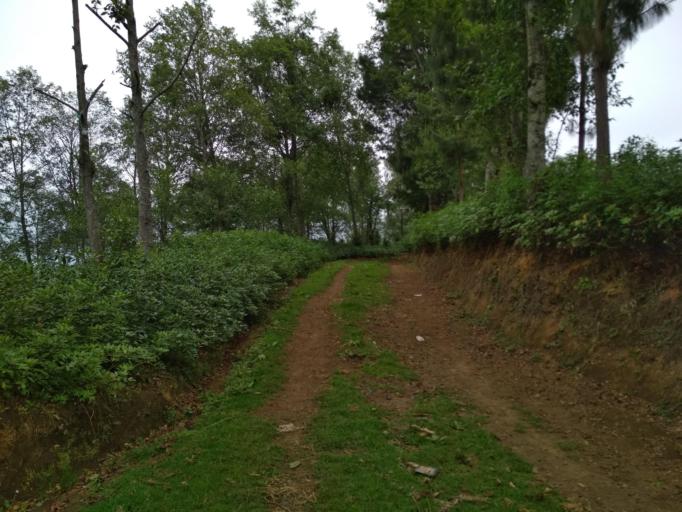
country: MX
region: Veracruz
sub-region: La Perla
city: Chilapa
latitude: 18.9928
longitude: -97.1680
